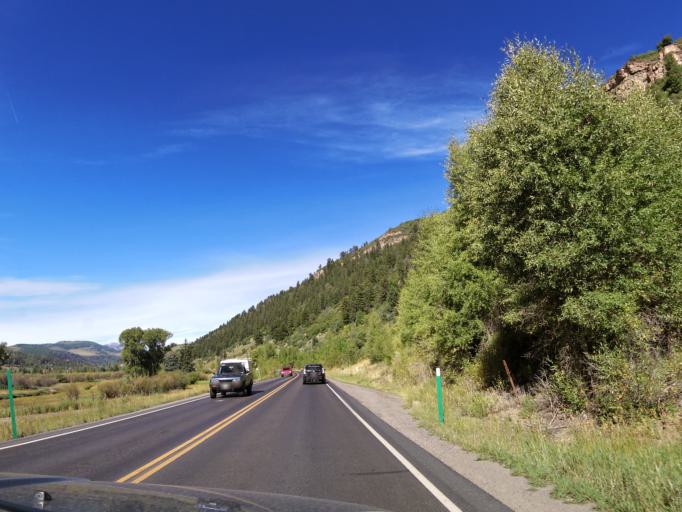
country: US
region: Colorado
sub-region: San Miguel County
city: Mountain Village
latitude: 37.9511
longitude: -107.8562
